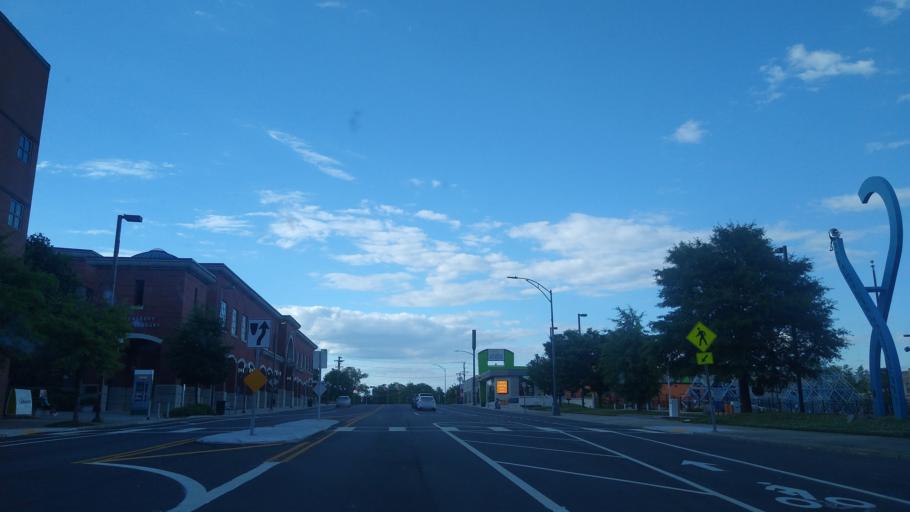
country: US
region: North Carolina
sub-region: Guilford County
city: Greensboro
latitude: 36.0739
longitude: -79.7867
